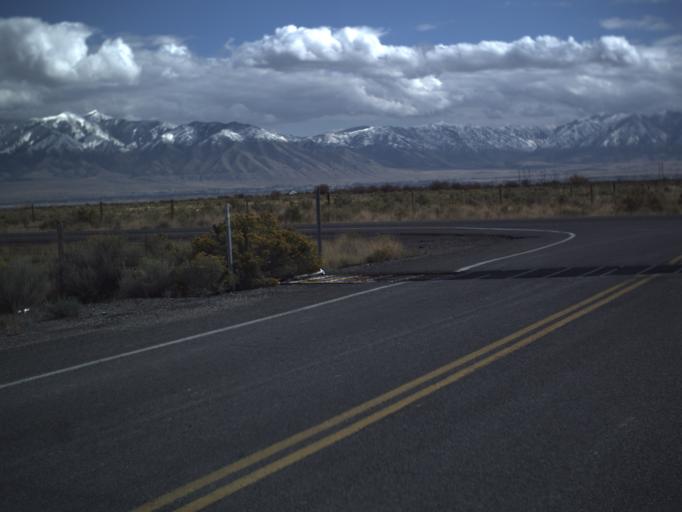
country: US
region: Utah
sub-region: Tooele County
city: Grantsville
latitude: 40.6808
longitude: -112.4437
